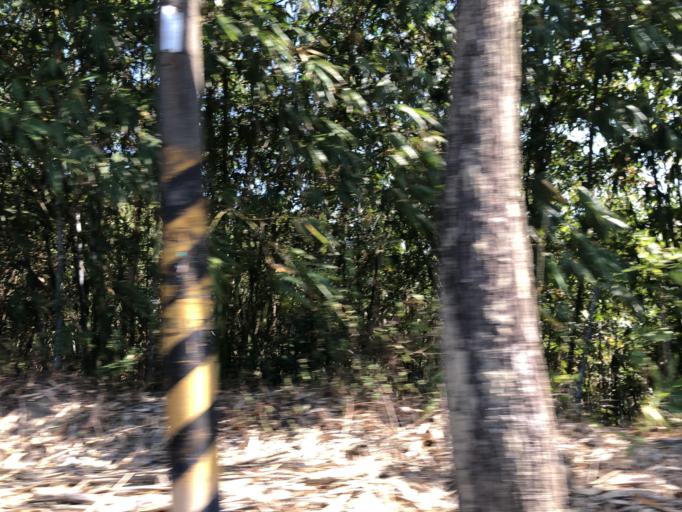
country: TW
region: Taiwan
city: Yujing
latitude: 23.0382
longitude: 120.3585
